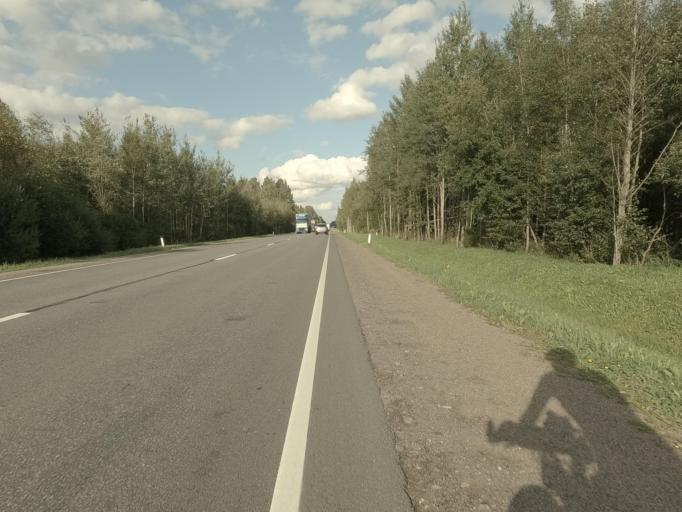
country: RU
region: Leningrad
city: Mga
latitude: 59.6869
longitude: 30.9648
